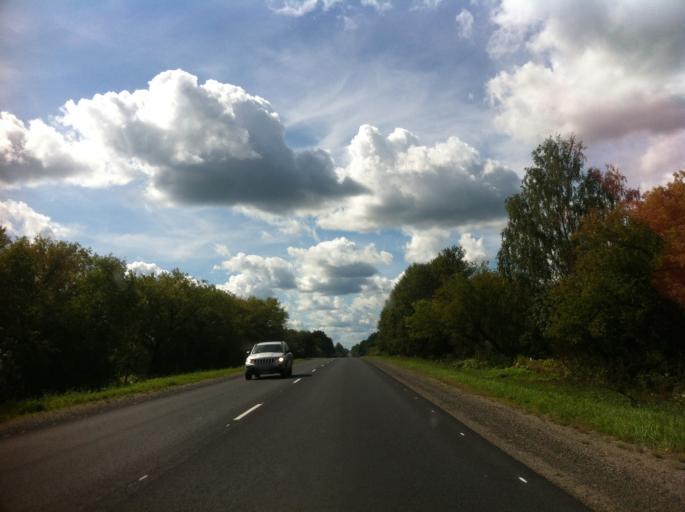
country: RU
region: Pskov
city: Izborsk
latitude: 57.7288
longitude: 27.9658
